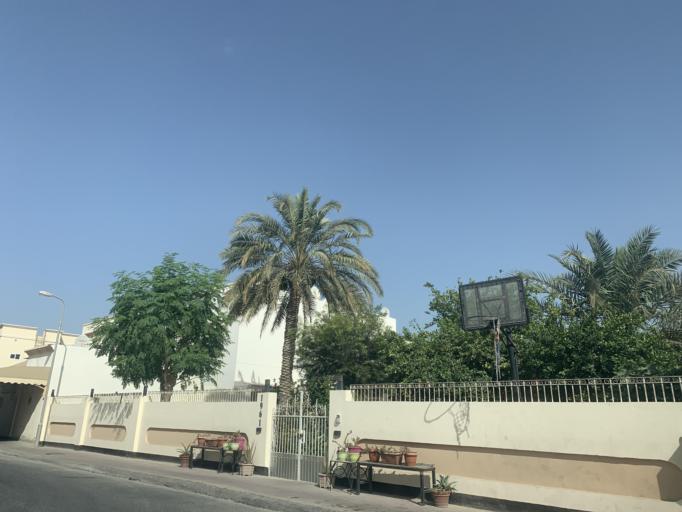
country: BH
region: Northern
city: Madinat `Isa
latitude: 26.1667
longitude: 50.5735
